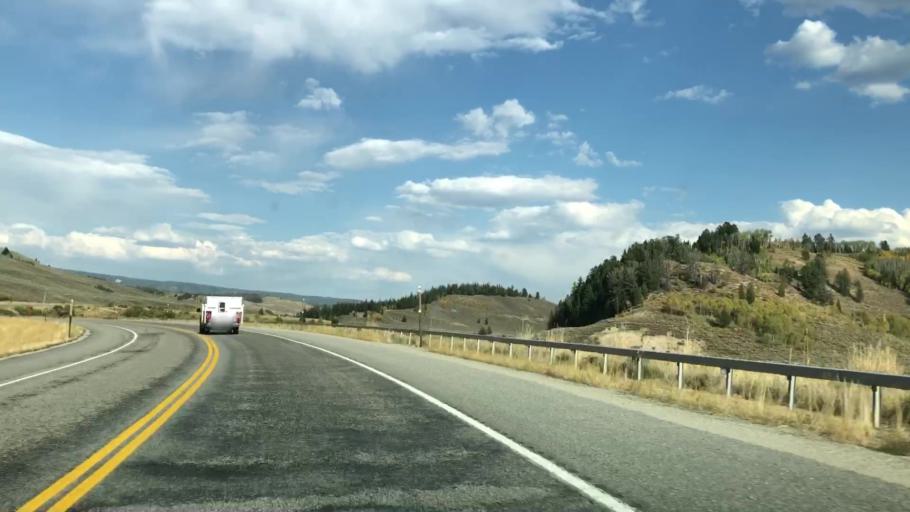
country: US
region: Wyoming
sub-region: Teton County
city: Hoback
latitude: 43.1529
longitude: -110.3367
